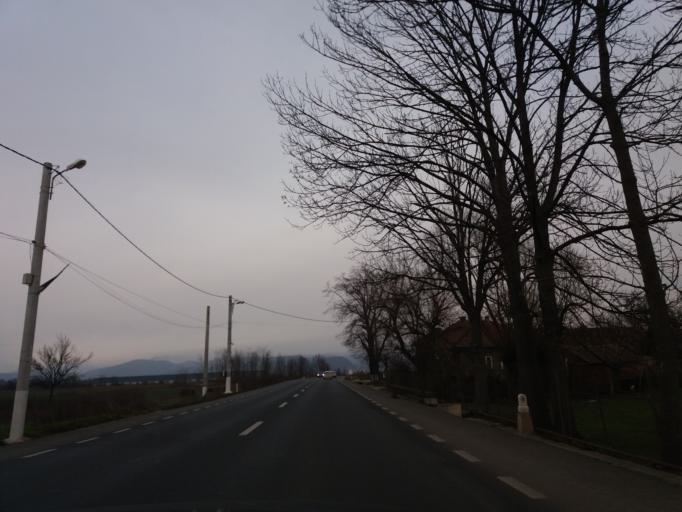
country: RO
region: Hunedoara
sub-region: Comuna Bacia
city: Bacia
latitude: 45.8066
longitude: 23.0141
